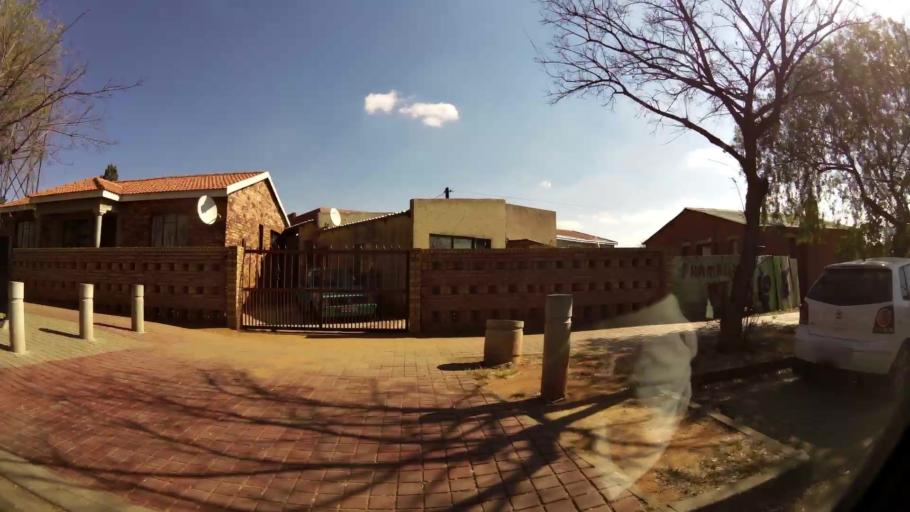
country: ZA
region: Gauteng
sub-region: City of Johannesburg Metropolitan Municipality
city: Soweto
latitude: -26.2376
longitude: 27.9065
